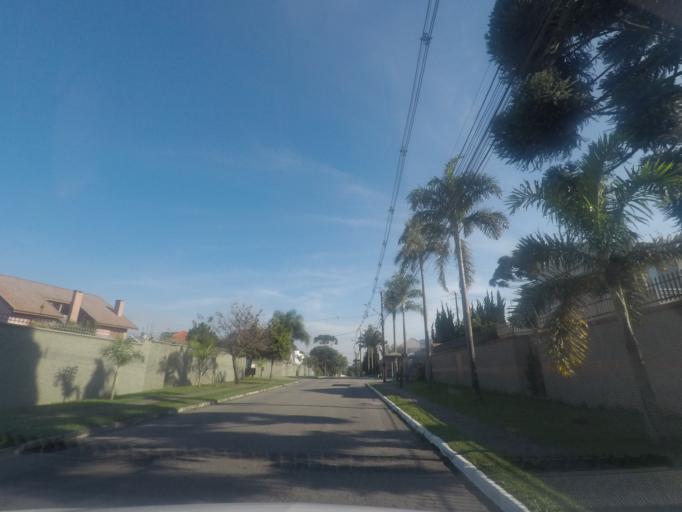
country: BR
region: Parana
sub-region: Pinhais
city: Pinhais
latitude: -25.4719
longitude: -49.2200
